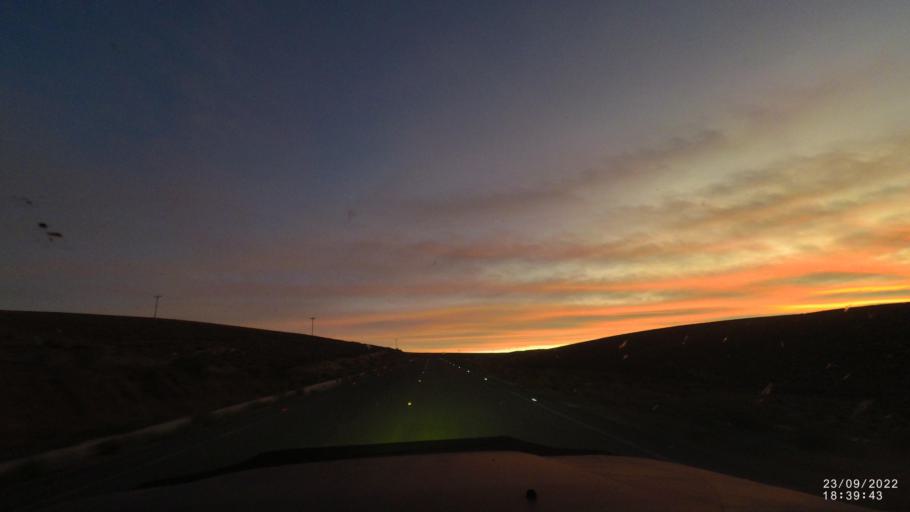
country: BO
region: Oruro
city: Challapata
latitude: -19.4208
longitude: -67.3325
